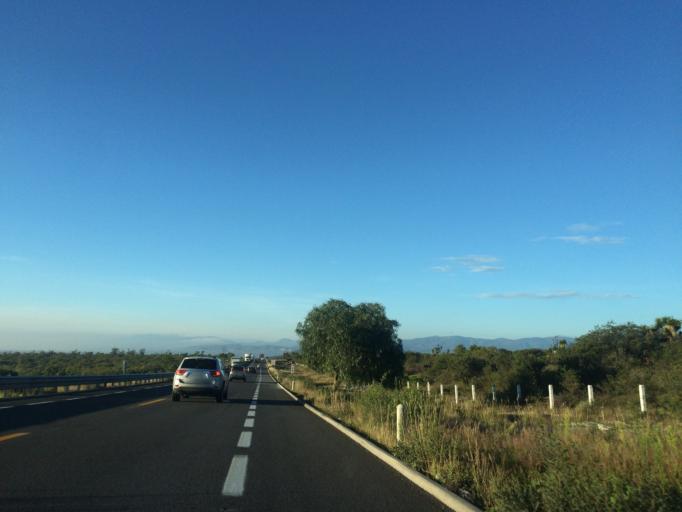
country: MX
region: Puebla
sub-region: Tehuacan
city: Magdalena Cuayucatepec
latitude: 18.6077
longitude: -97.4753
